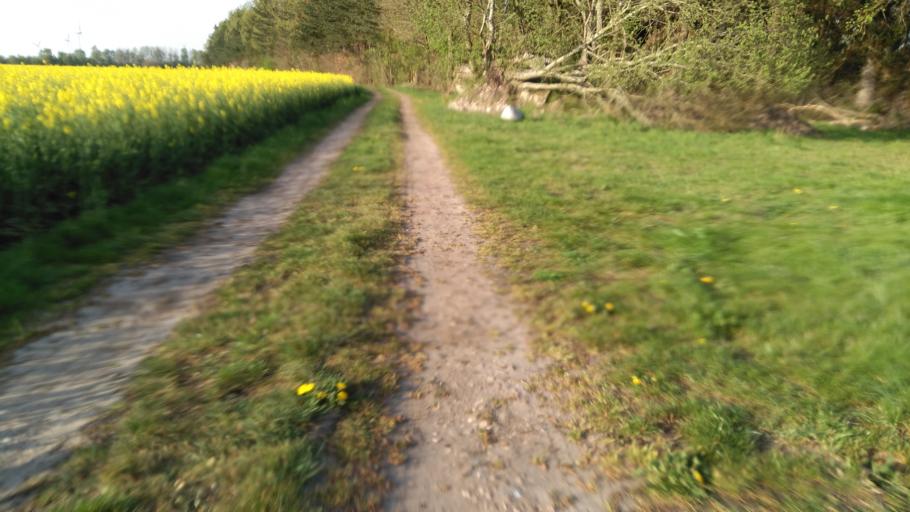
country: DE
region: Lower Saxony
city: Apensen
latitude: 53.4377
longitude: 9.5820
